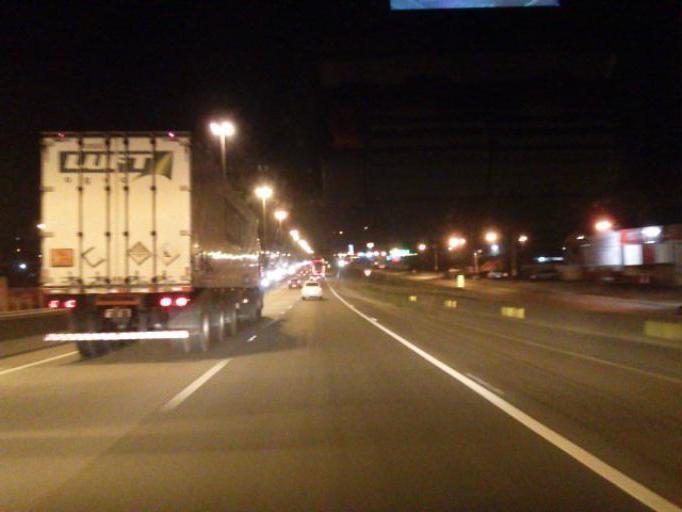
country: BR
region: Santa Catarina
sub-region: Balneario Camboriu
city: Balneario Camboriu
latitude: -27.0196
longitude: -48.6099
